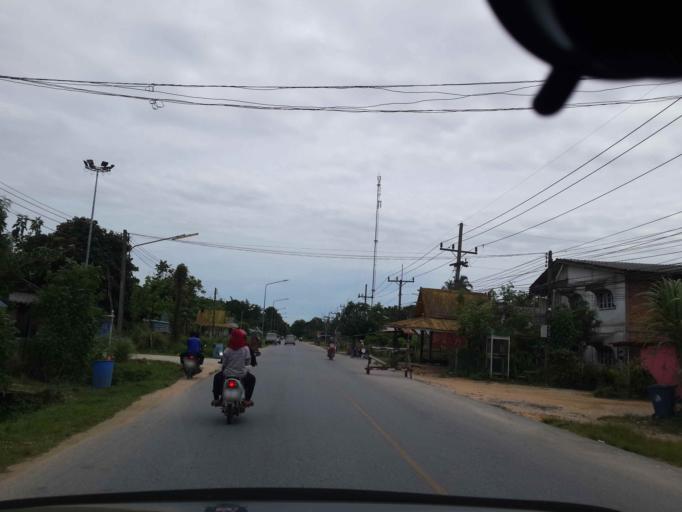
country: TH
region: Narathiwat
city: Ra-ngae
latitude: 6.3341
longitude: 101.6464
